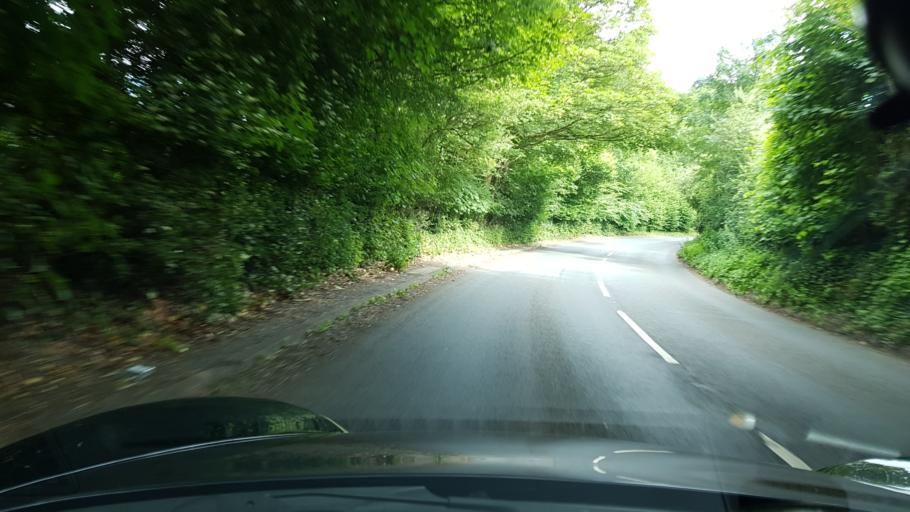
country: GB
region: Wales
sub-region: Monmouthshire
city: Abergavenny
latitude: 51.8174
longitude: -3.0429
